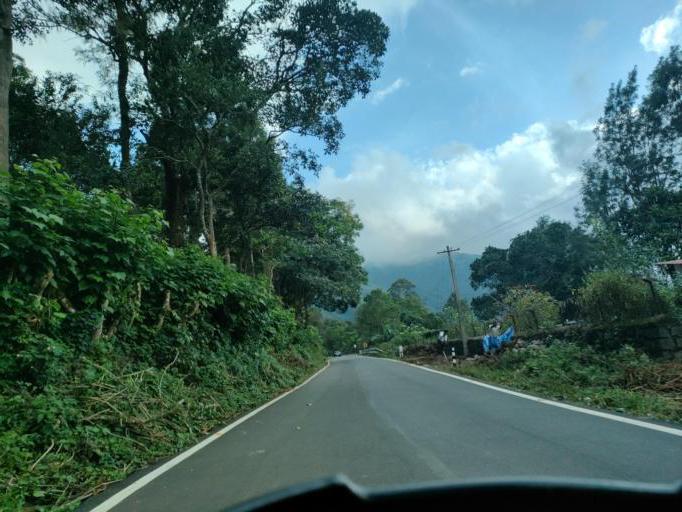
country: IN
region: Tamil Nadu
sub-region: Dindigul
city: Kodaikanal
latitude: 10.2696
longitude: 77.5338
